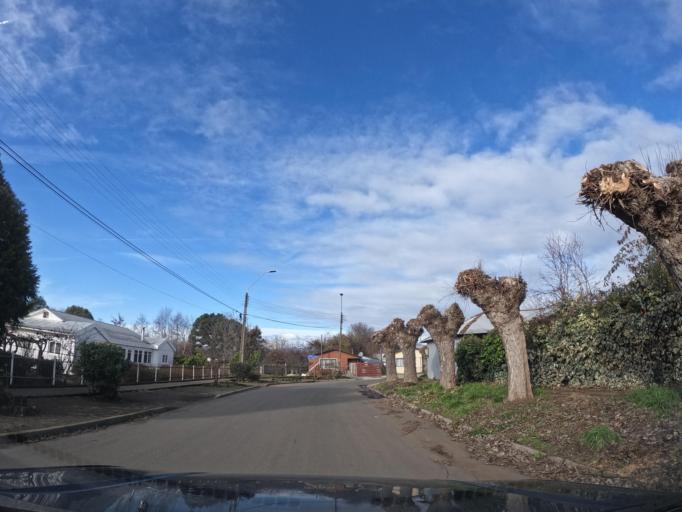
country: CL
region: Biobio
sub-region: Provincia de Nuble
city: Coihueco
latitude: -36.7043
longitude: -71.8869
